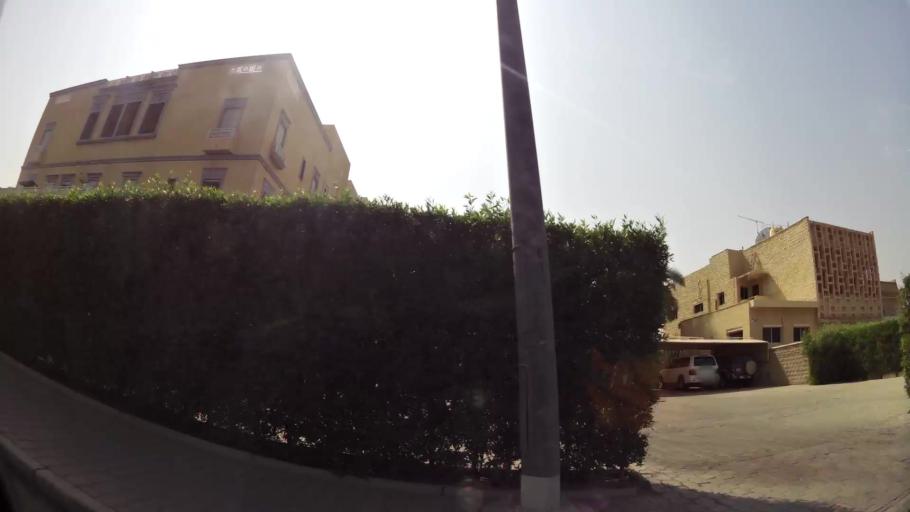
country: KW
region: Al Asimah
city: Ad Dasmah
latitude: 29.3635
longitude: 48.0142
